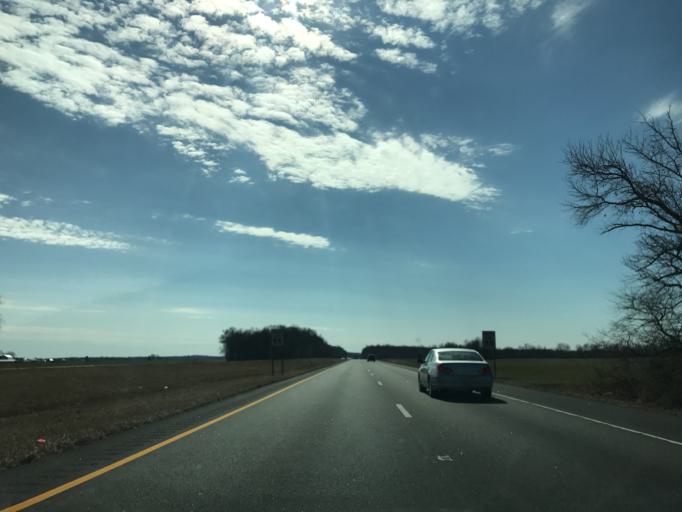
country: US
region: Maryland
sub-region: Queen Anne's County
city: Kingstown
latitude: 39.1691
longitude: -75.9186
